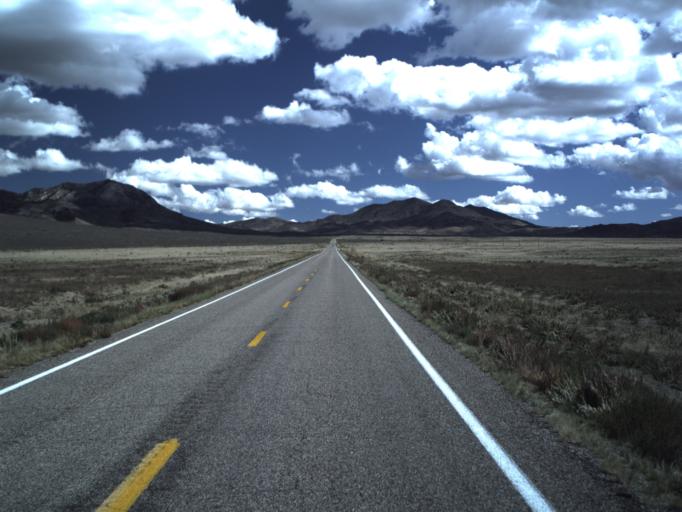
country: US
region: Utah
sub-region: Beaver County
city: Milford
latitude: 38.4566
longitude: -113.3643
